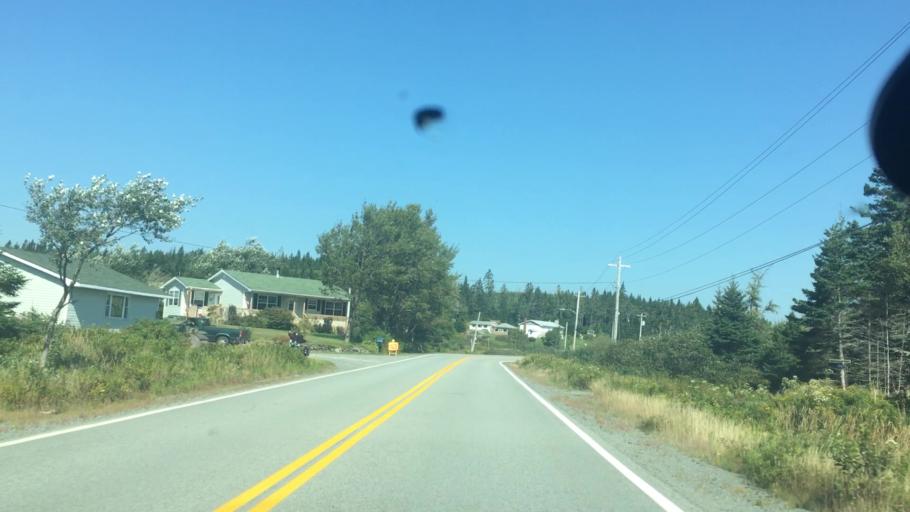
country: CA
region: Nova Scotia
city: New Glasgow
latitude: 44.9259
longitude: -62.2983
